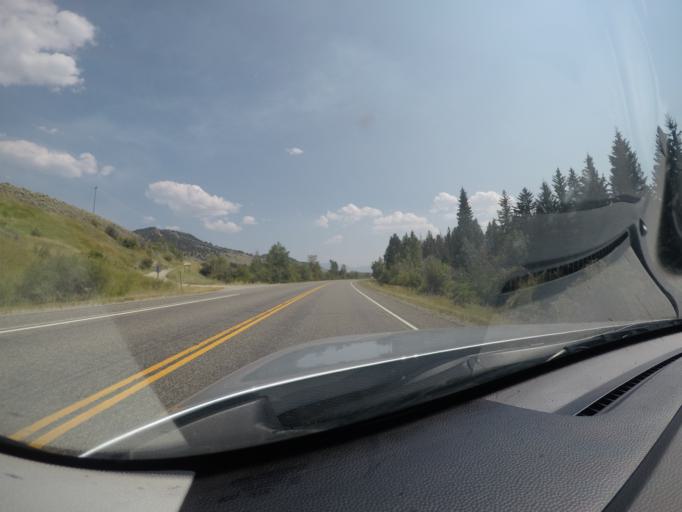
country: US
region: Montana
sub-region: Gallatin County
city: Big Sky
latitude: 44.8981
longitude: -111.5867
